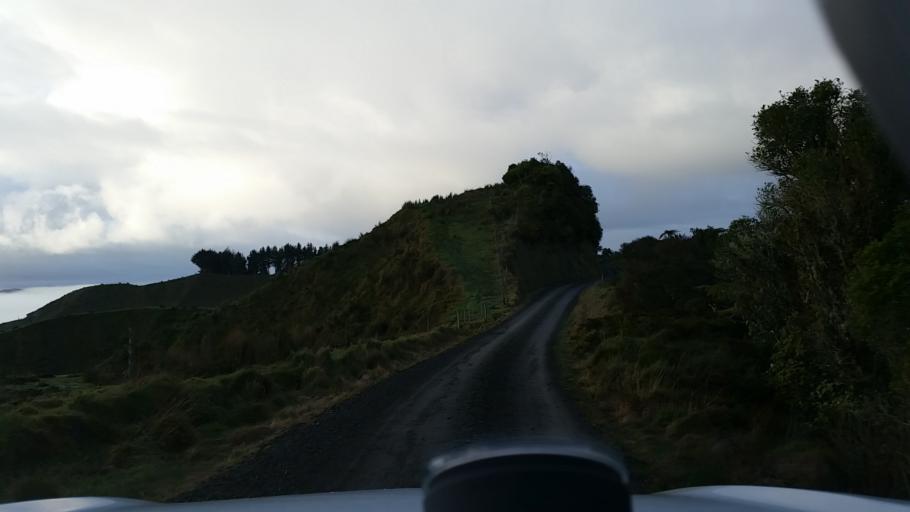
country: NZ
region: Taranaki
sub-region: South Taranaki District
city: Eltham
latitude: -39.4449
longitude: 174.4526
